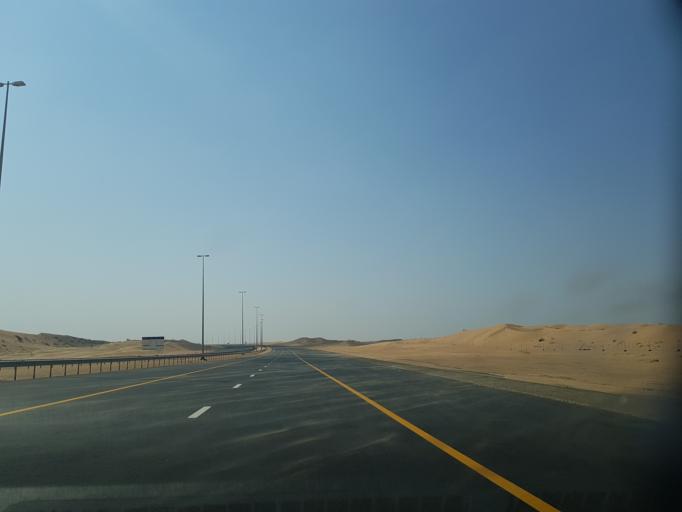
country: AE
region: Ash Shariqah
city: Adh Dhayd
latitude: 25.2689
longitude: 55.6538
